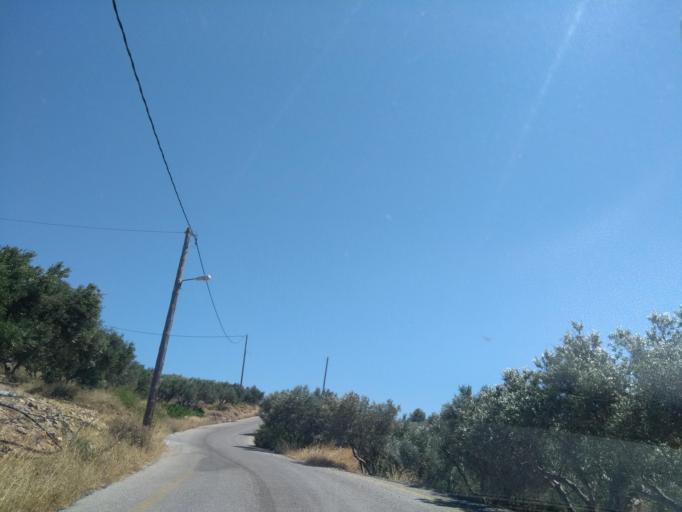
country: GR
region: Crete
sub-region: Nomos Chanias
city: Vryses
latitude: 35.3606
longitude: 23.5402
